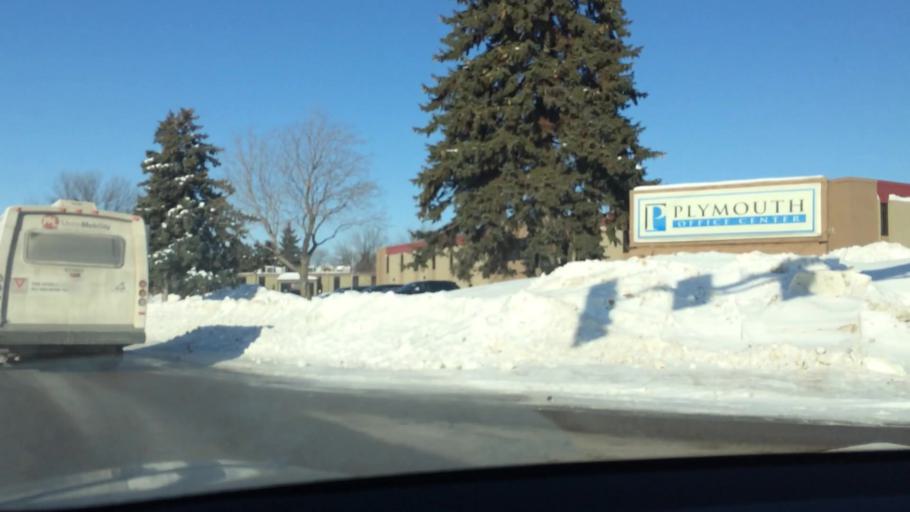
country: US
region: Minnesota
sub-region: Hennepin County
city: Plymouth
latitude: 45.0142
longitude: -93.4616
